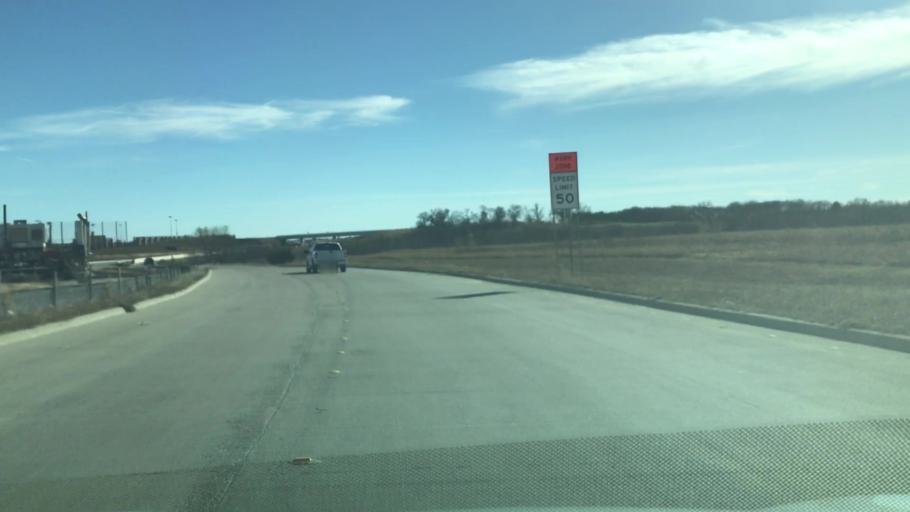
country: US
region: Texas
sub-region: Tarrant County
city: Mansfield
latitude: 32.5605
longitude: -97.0878
